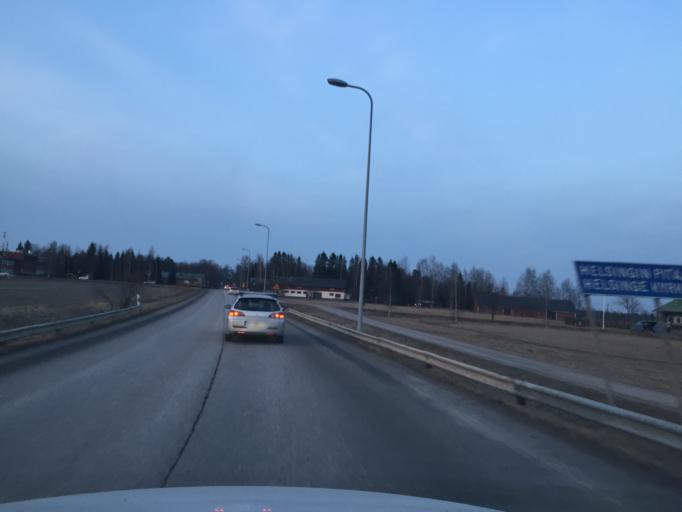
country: FI
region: Uusimaa
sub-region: Helsinki
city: Vantaa
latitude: 60.2793
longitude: 24.9802
